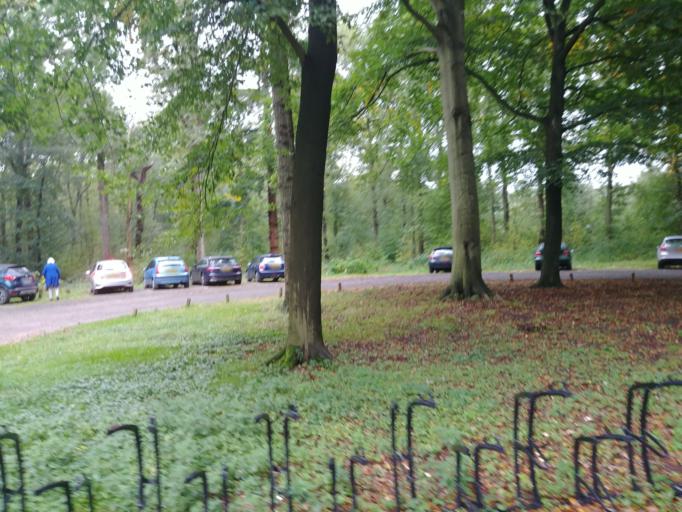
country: NL
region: North Holland
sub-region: Gemeente Heemstede
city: Heemstede
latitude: 52.3756
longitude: 4.5903
